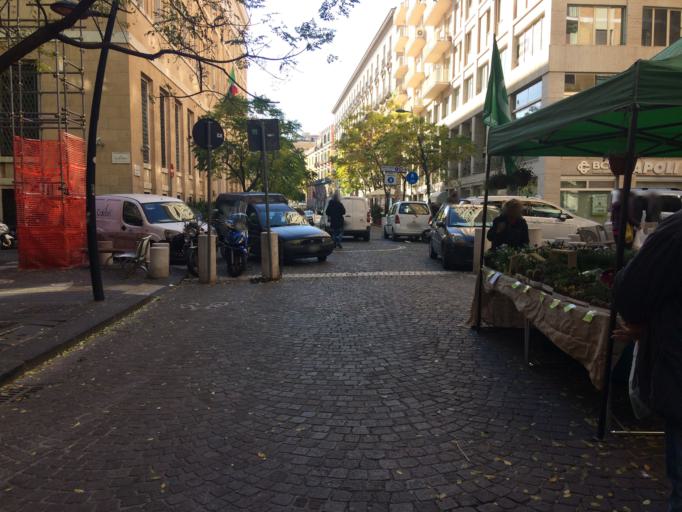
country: IT
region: Campania
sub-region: Provincia di Napoli
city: Napoli
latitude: 40.8412
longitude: 14.2510
